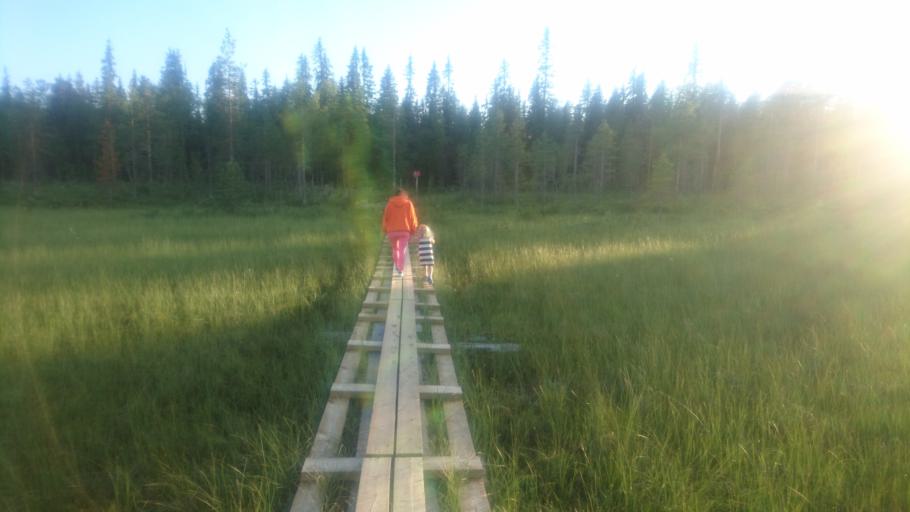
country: SE
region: Norrbotten
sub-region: Arvidsjaurs Kommun
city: Arvidsjaur
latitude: 65.7808
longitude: 19.4871
